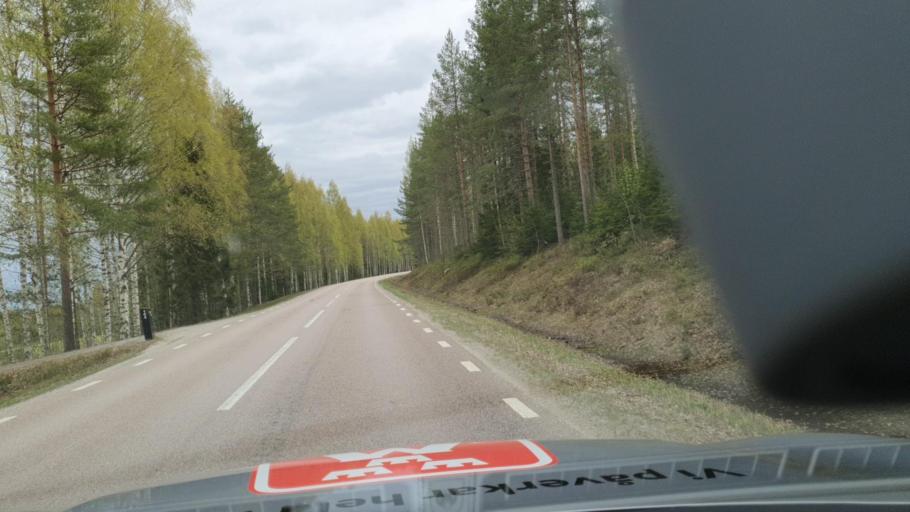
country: SE
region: Vaesternorrland
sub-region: OErnskoeldsviks Kommun
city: Ornskoldsvik
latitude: 63.4956
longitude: 18.8677
